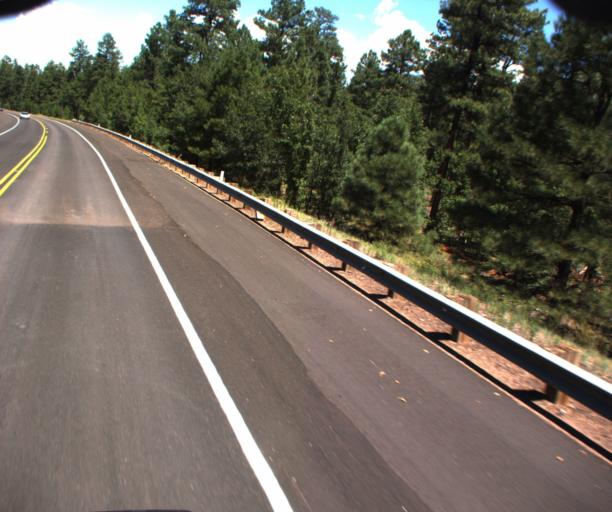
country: US
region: Arizona
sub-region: Navajo County
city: Show Low
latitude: 34.2146
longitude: -110.0736
